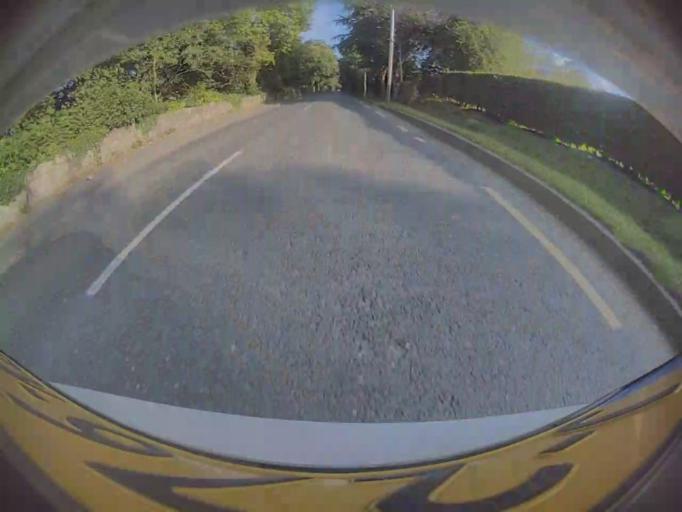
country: IE
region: Leinster
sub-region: Wicklow
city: Enniskerry
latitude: 53.2262
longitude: -6.1835
